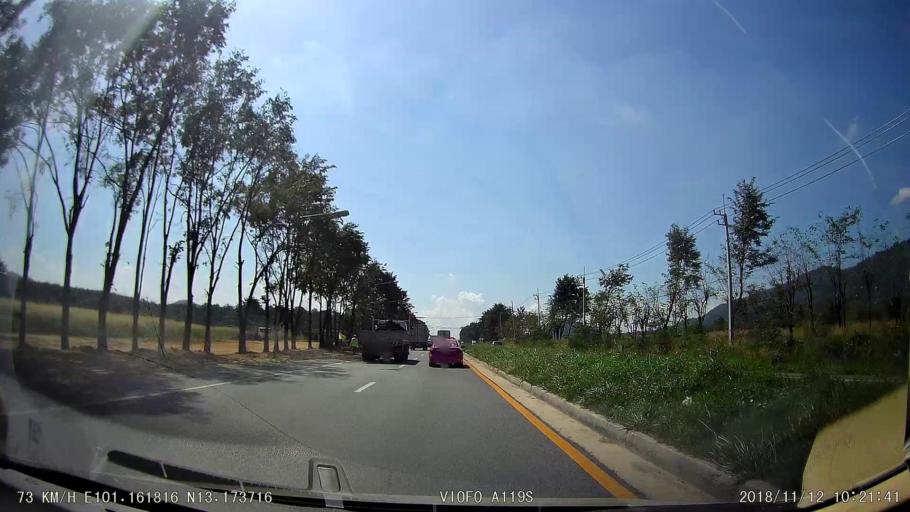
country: TH
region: Chon Buri
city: Ban Bueng
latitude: 13.1734
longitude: 101.1618
